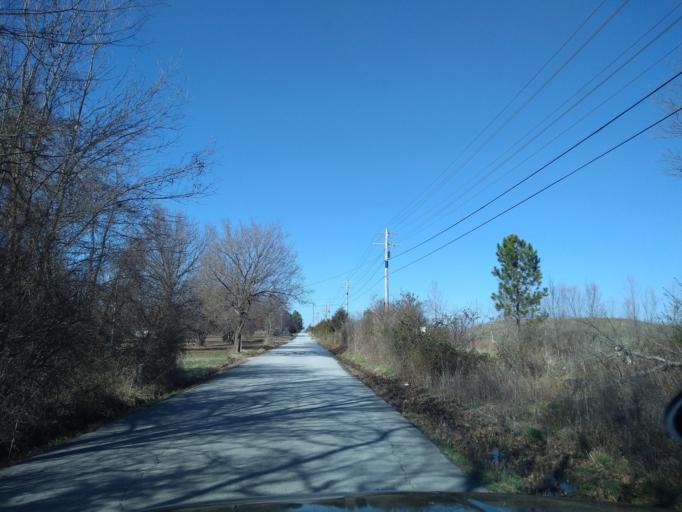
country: US
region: Arkansas
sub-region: Washington County
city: Farmington
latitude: 36.0626
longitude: -94.2401
